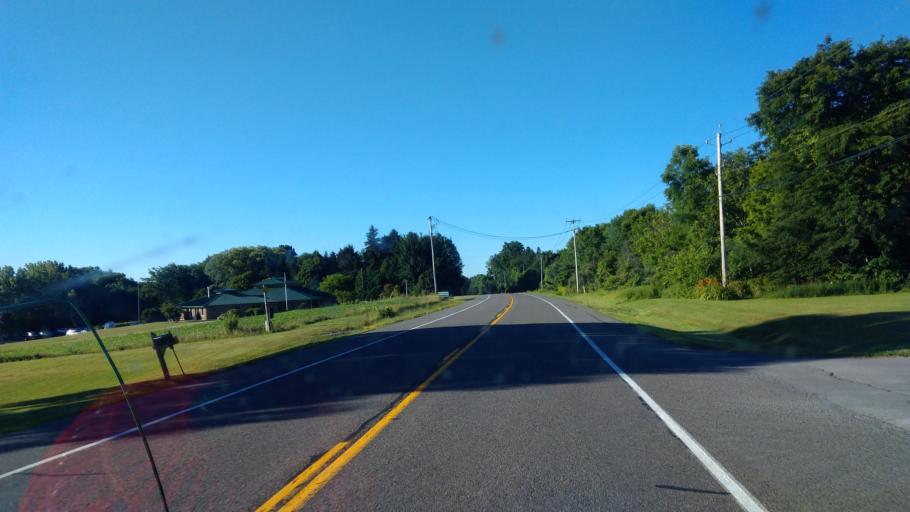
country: US
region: New York
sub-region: Ontario County
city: Phelps
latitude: 42.9641
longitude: -76.9776
